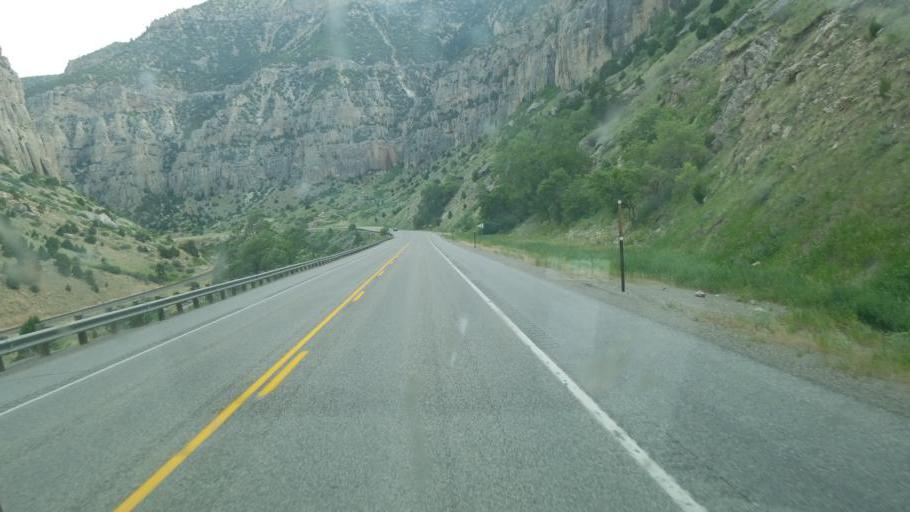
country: US
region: Wyoming
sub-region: Hot Springs County
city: Thermopolis
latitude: 43.5203
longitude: -108.1792
